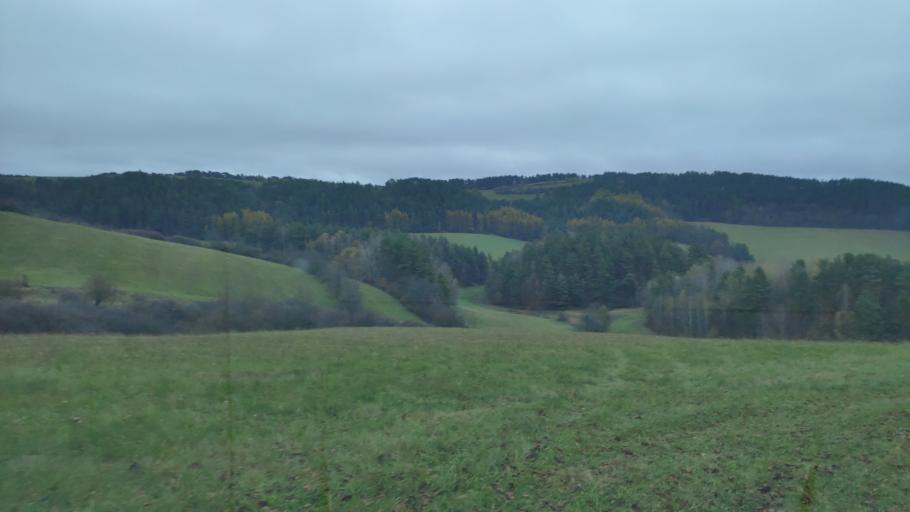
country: SK
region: Presovsky
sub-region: Okres Presov
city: Presov
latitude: 48.9280
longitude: 21.0982
